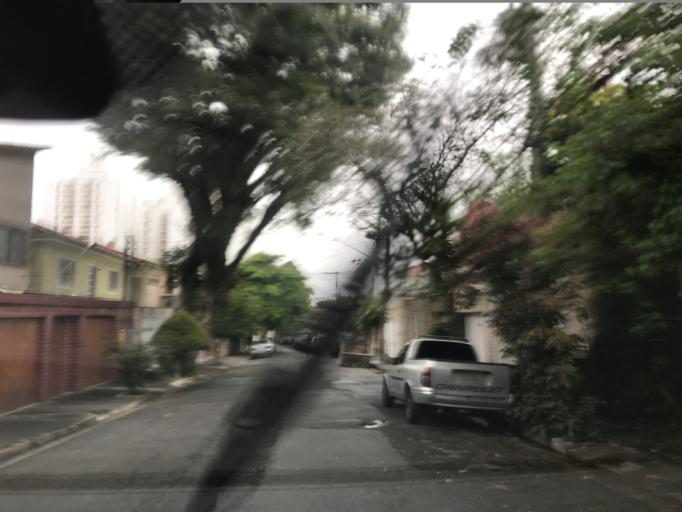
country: BR
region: Sao Paulo
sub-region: Sao Paulo
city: Sao Paulo
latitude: -23.5427
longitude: -46.6797
